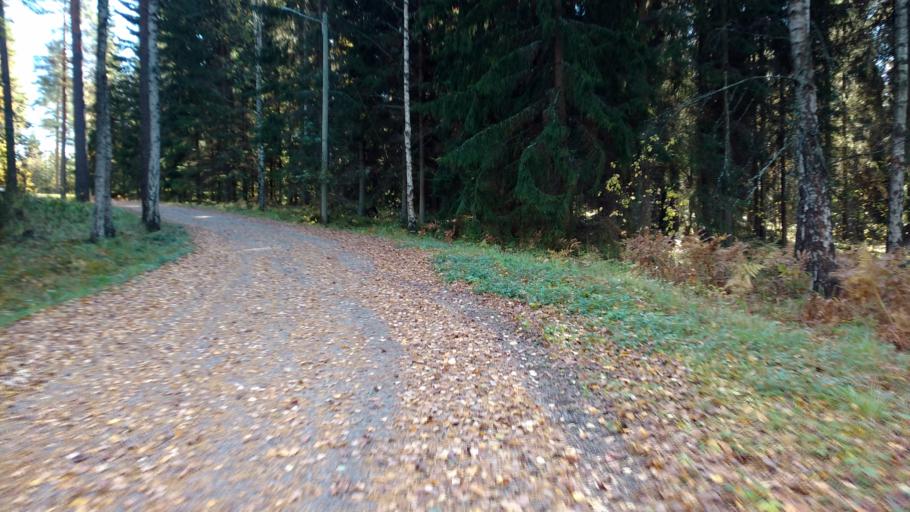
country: FI
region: Varsinais-Suomi
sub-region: Salo
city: Salo
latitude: 60.3961
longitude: 23.1752
